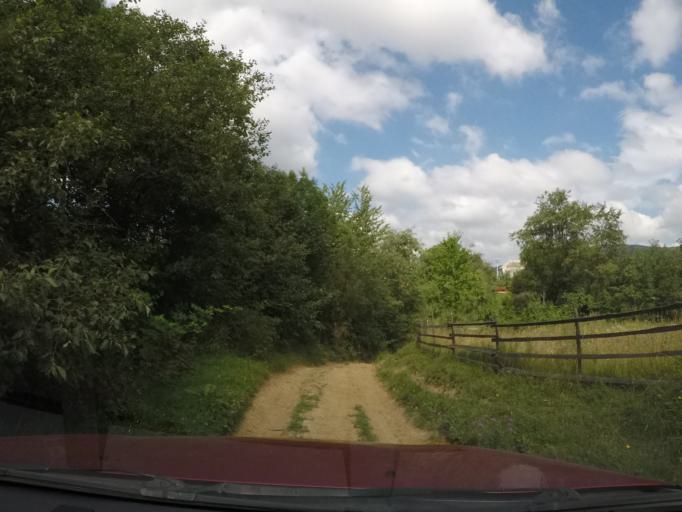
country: UA
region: Zakarpattia
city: Velykyi Bereznyi
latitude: 48.9447
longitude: 22.6843
